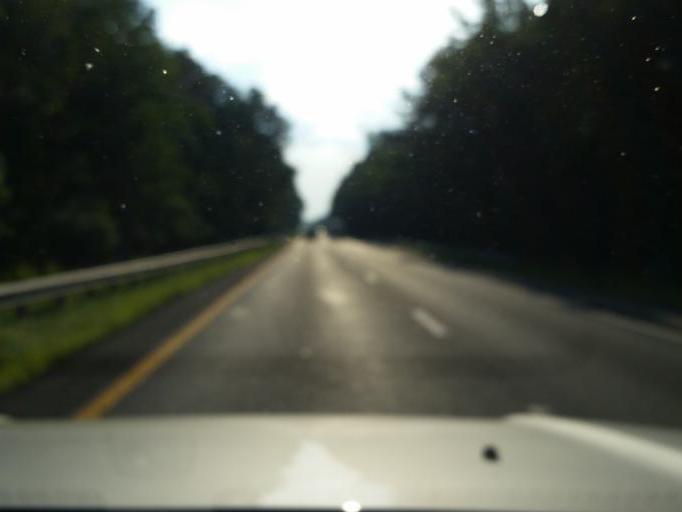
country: US
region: Virginia
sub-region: New Kent County
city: New Kent
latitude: 37.4956
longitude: -77.0220
